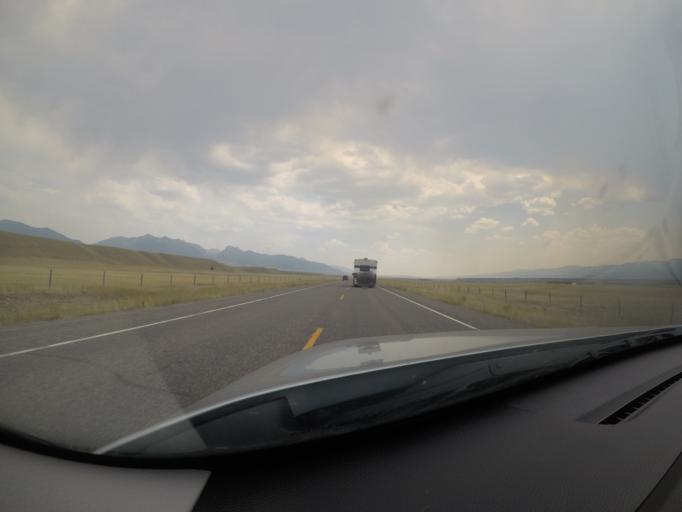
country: US
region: Montana
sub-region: Madison County
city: Virginia City
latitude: 45.1314
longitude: -111.6690
